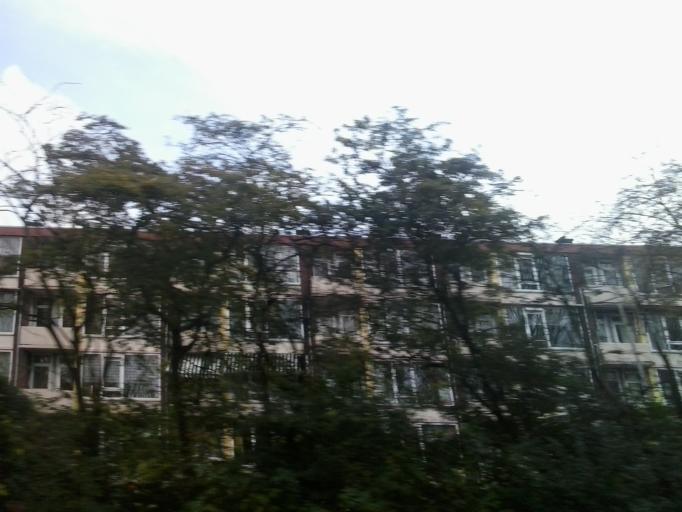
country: NL
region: South Holland
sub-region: Gemeente Delft
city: Delft
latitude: 52.0029
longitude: 4.3480
